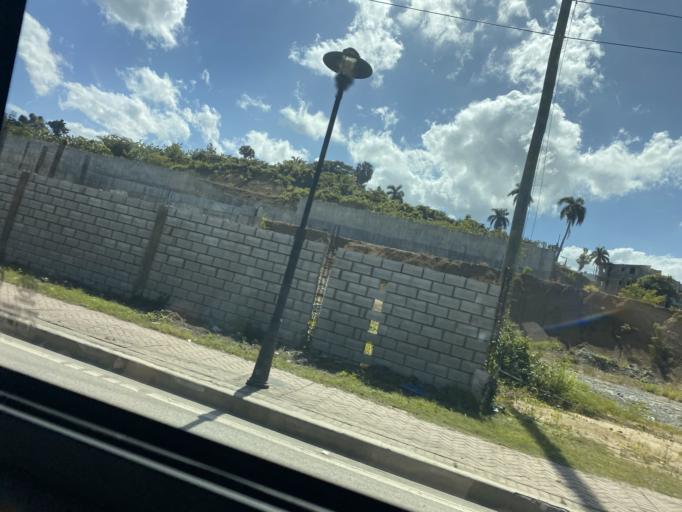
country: DO
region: Puerto Plata
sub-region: Puerto Plata
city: Puerto Plata
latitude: 19.7938
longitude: -70.7119
